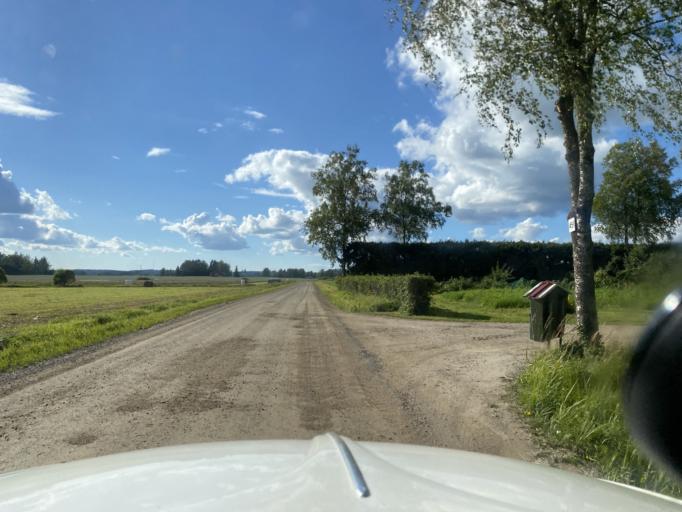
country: FI
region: Pirkanmaa
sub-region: Lounais-Pirkanmaa
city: Punkalaidun
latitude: 61.1291
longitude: 23.2454
